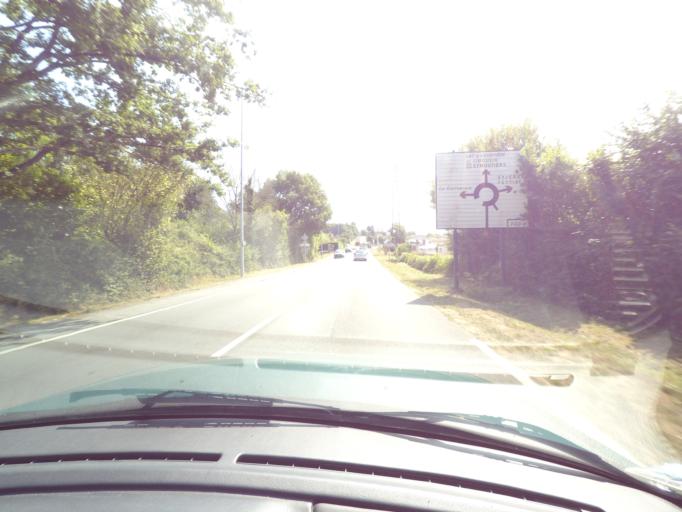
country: FR
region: Limousin
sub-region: Departement de la Haute-Vienne
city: Feytiat
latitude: 45.8146
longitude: 1.3178
